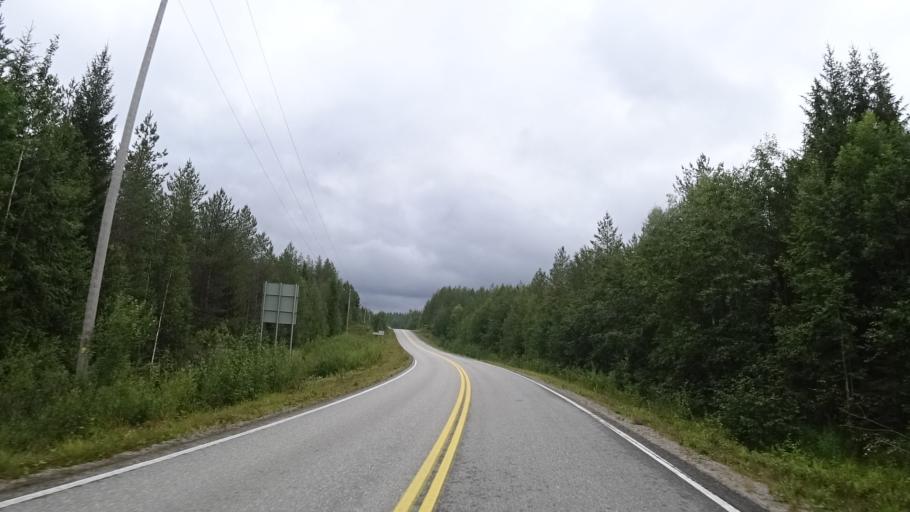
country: FI
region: North Karelia
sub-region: Joensuu
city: Ilomantsi
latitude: 63.2502
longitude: 30.7133
